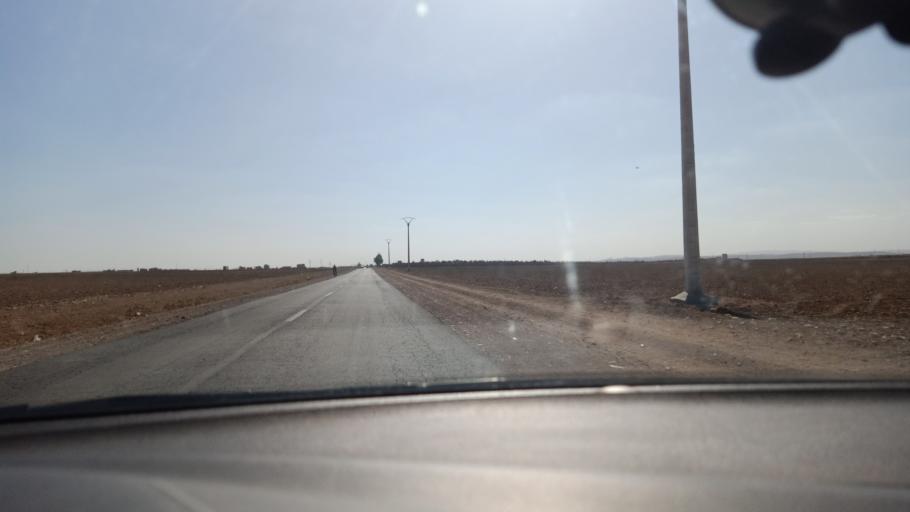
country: MA
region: Doukkala-Abda
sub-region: Safi
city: Youssoufia
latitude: 32.1272
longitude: -8.6010
